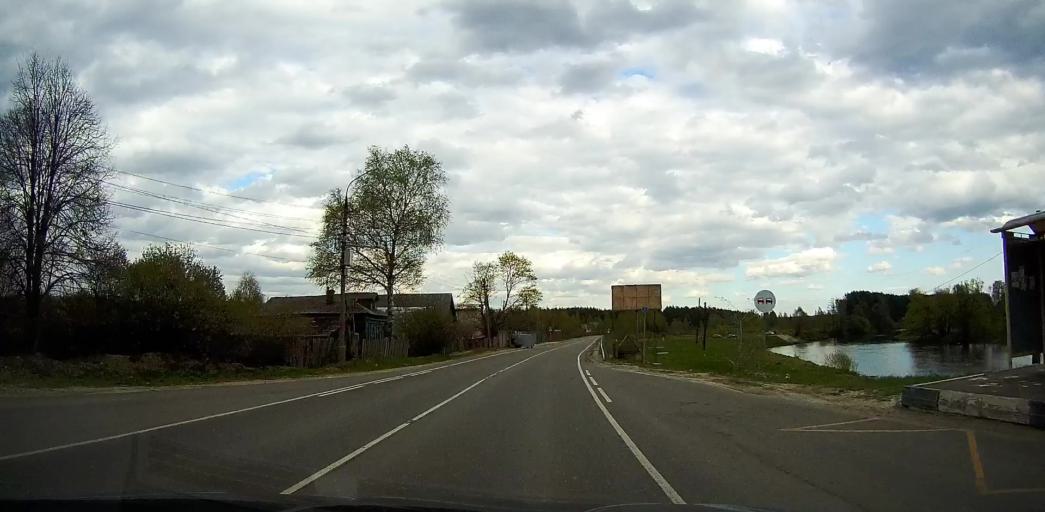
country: RU
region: Moskovskaya
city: Pavlovskiy Posad
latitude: 55.8024
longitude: 38.6681
